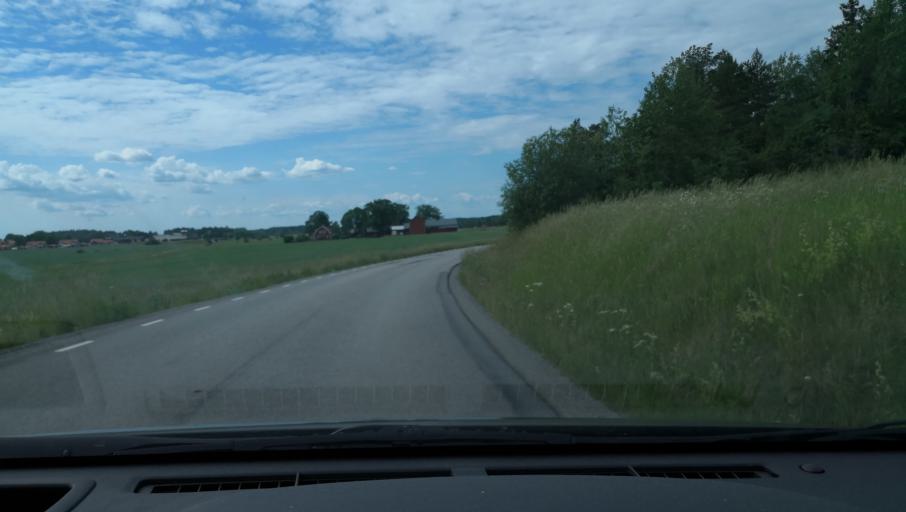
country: SE
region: Uppsala
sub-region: Uppsala Kommun
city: Uppsala
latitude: 59.8101
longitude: 17.5143
